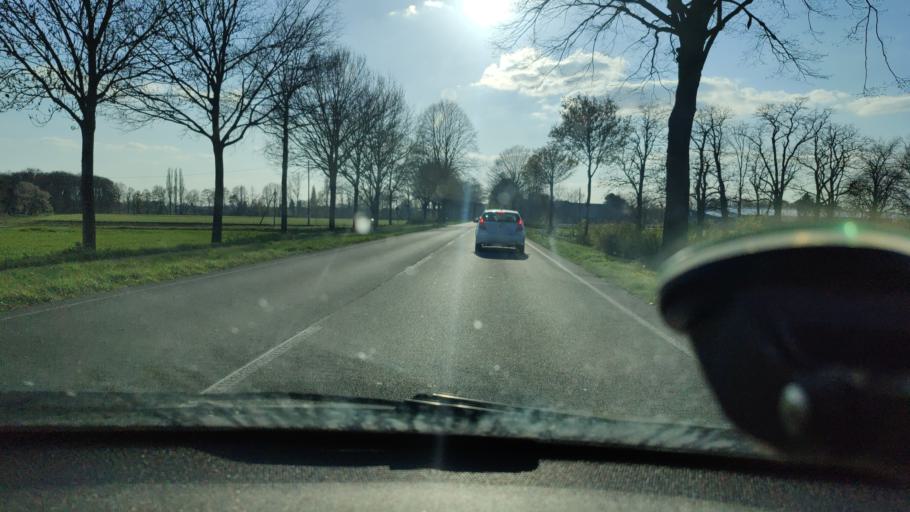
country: DE
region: North Rhine-Westphalia
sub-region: Regierungsbezirk Dusseldorf
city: Hunxe
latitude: 51.6805
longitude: 6.8130
